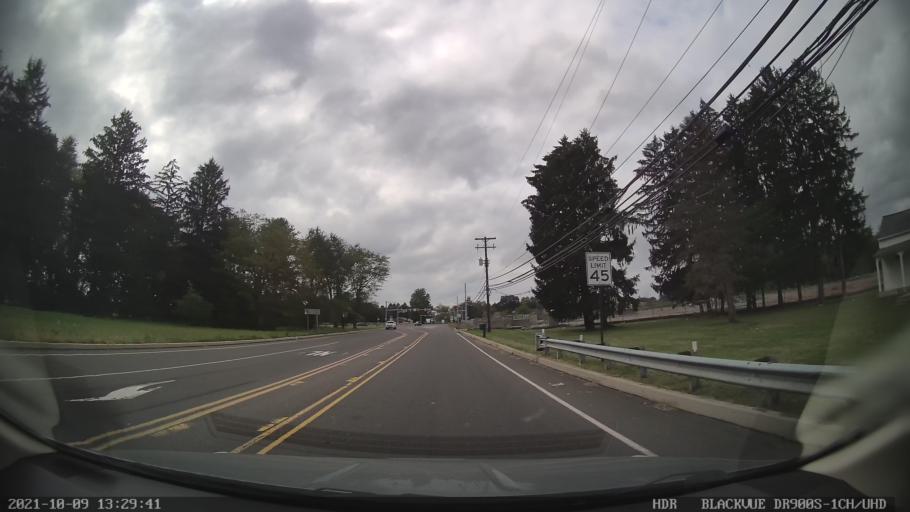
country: US
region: Pennsylvania
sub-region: Lehigh County
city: Trexlertown
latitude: 40.5337
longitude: -75.6026
